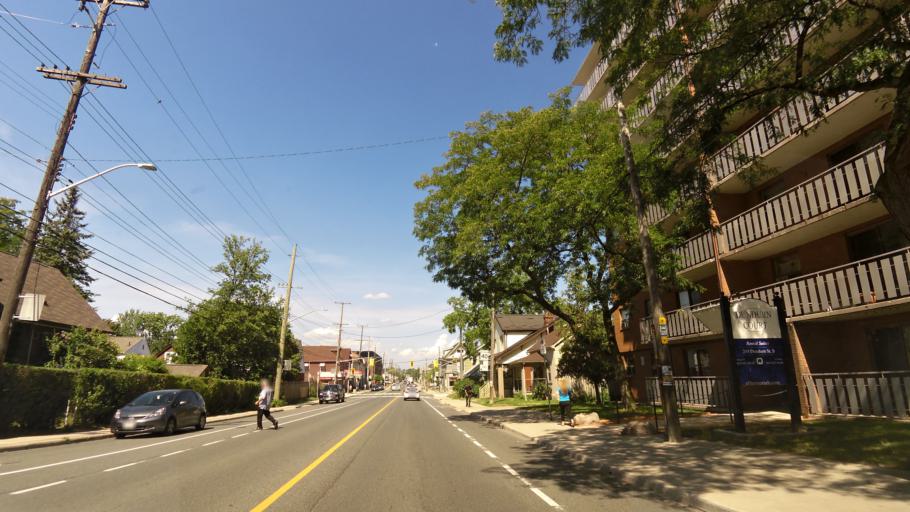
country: CA
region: Ontario
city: Hamilton
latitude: 43.2521
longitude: -79.8920
